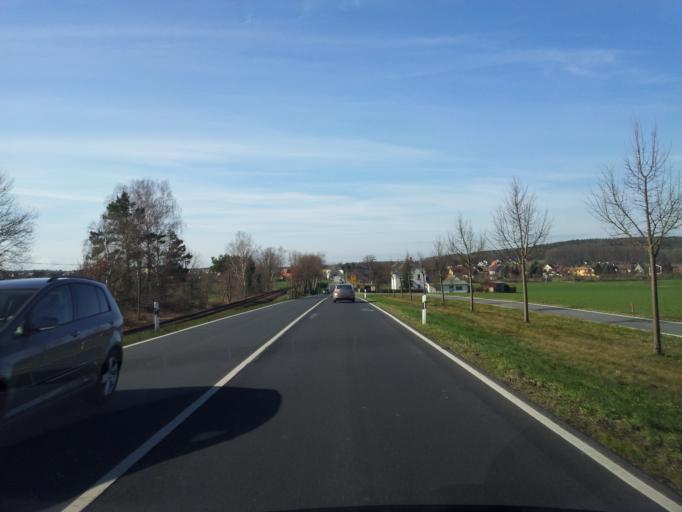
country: DE
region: Saxony
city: Laussnitz
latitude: 51.2531
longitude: 13.8857
